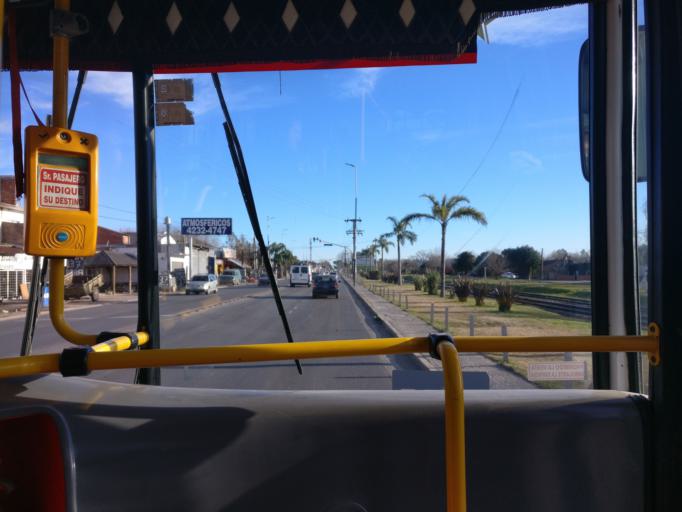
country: AR
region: Buenos Aires
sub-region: Partido de Ezeiza
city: Ezeiza
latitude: -34.8634
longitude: -58.5343
